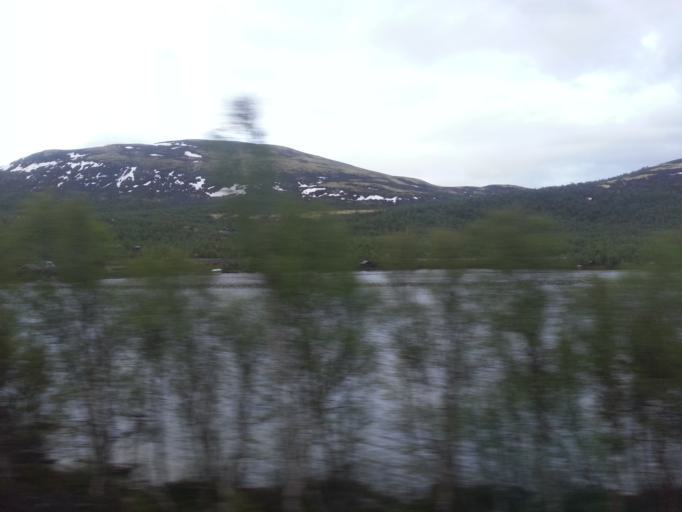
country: NO
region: Oppland
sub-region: Dovre
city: Dovre
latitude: 62.1764
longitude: 9.4218
